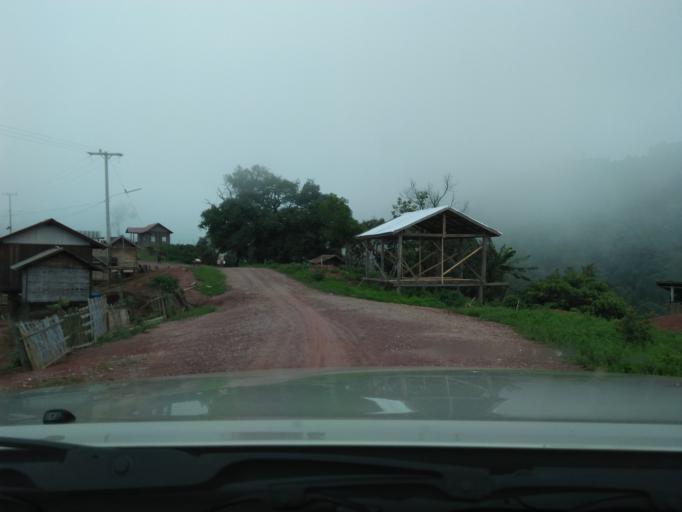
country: TH
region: Nan
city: Bo Kluea
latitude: 19.3847
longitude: 101.2383
